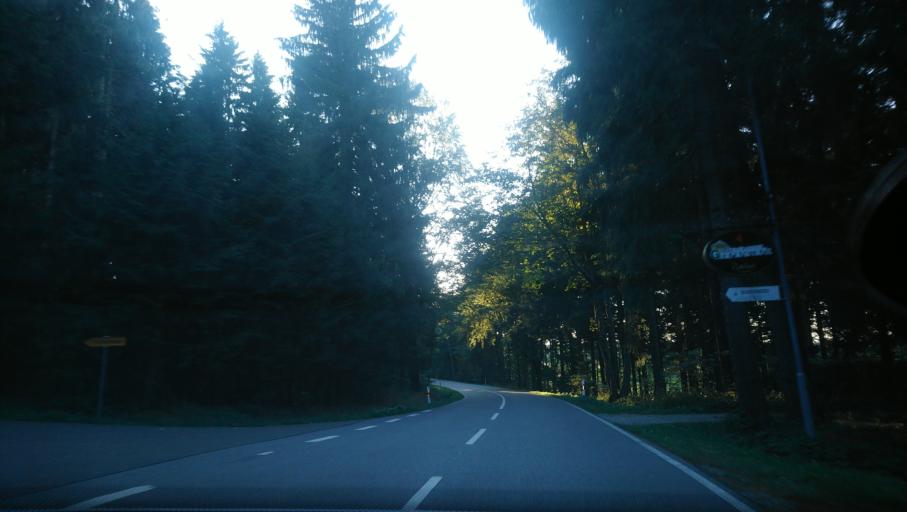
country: DE
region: Saxony
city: Thum
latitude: 50.6531
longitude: 12.9292
